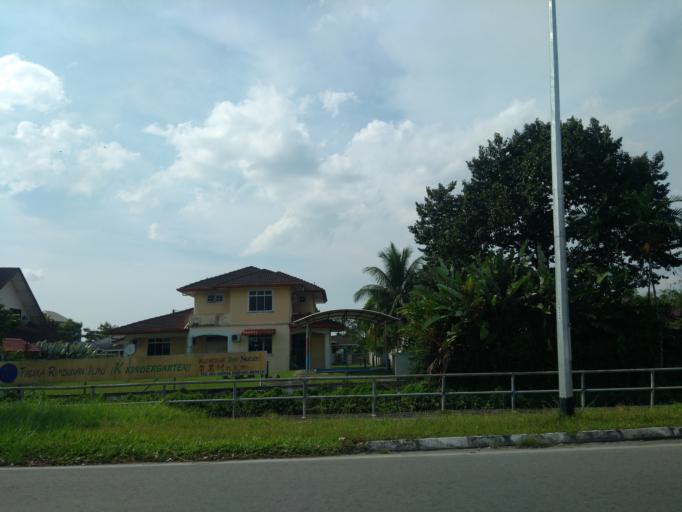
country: MY
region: Sarawak
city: Kuching
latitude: 1.5732
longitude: 110.2986
